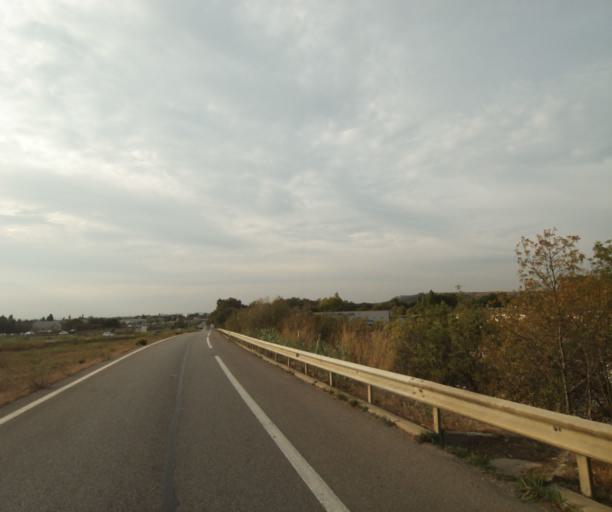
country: FR
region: Provence-Alpes-Cote d'Azur
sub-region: Departement des Bouches-du-Rhone
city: Les Pennes-Mirabeau
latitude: 43.4170
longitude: 5.2769
